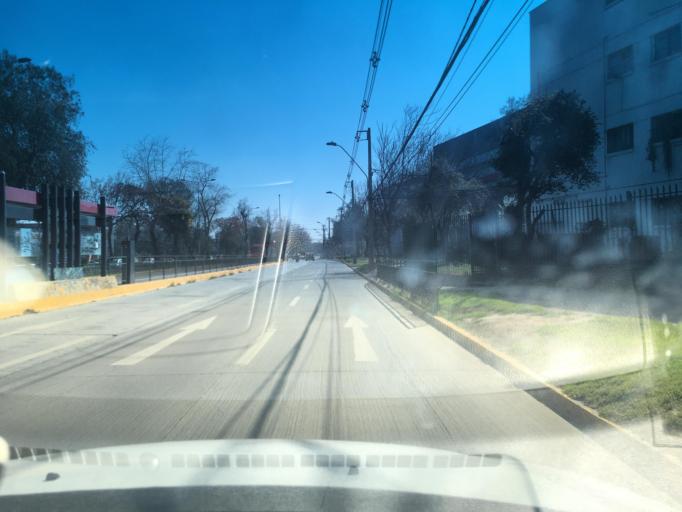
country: CL
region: Santiago Metropolitan
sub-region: Provincia de Santiago
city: Villa Presidente Frei, Nunoa, Santiago, Chile
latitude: -33.4676
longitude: -70.5802
